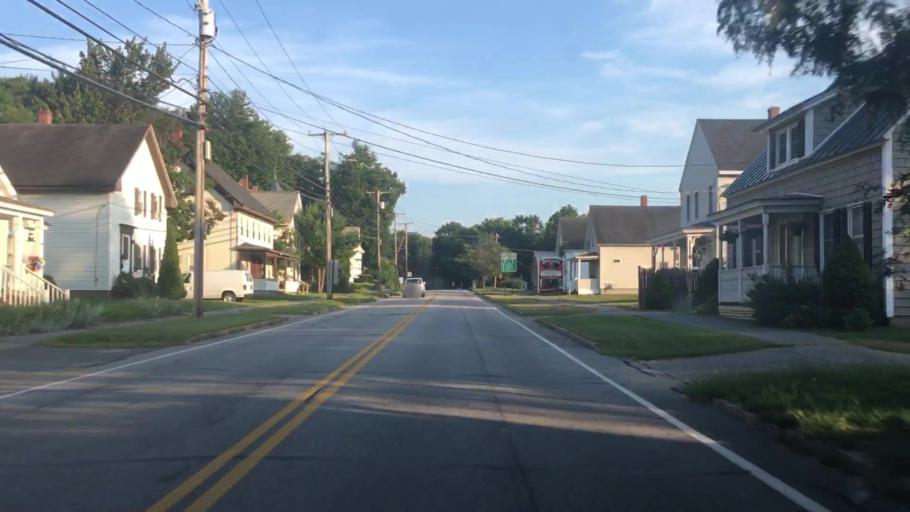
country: US
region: New Hampshire
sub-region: Belknap County
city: Laconia
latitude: 43.5198
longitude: -71.4649
